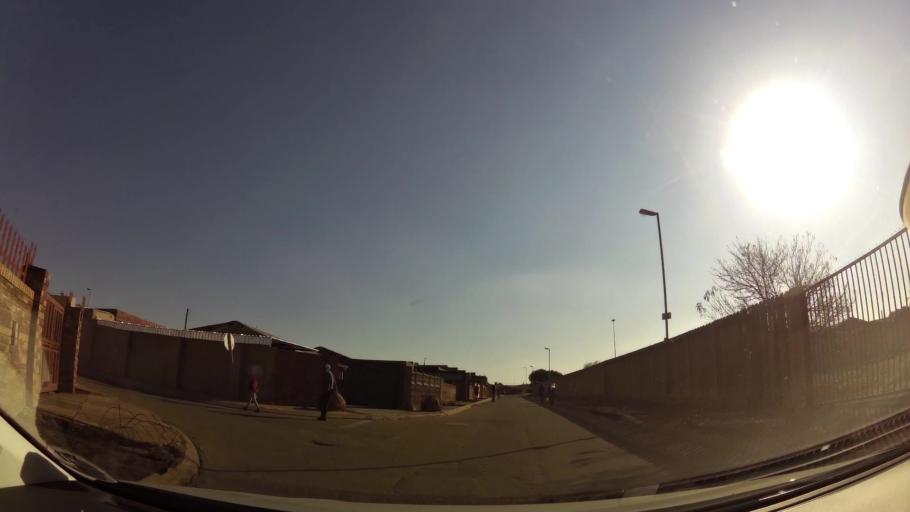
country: ZA
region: Gauteng
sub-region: City of Johannesburg Metropolitan Municipality
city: Soweto
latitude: -26.2730
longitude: 27.8798
